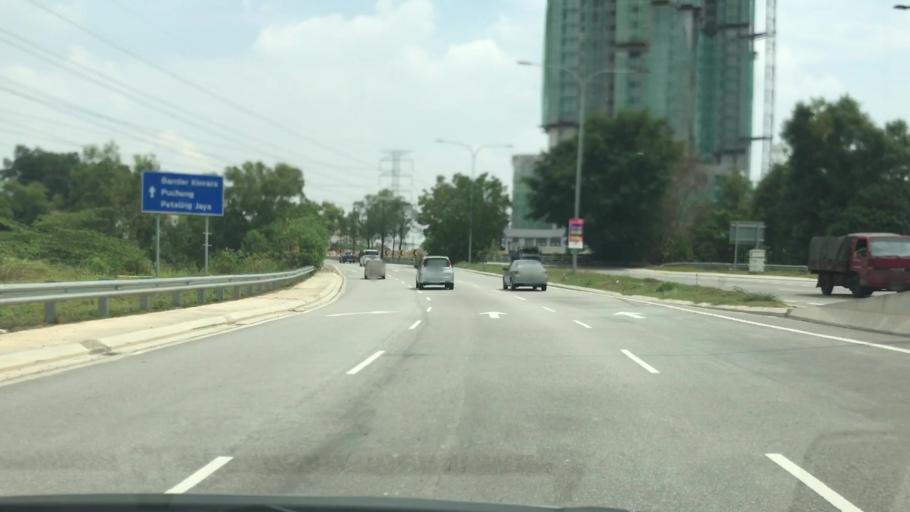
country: MY
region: Selangor
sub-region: Petaling
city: Petaling Jaya
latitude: 3.0546
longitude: 101.6674
